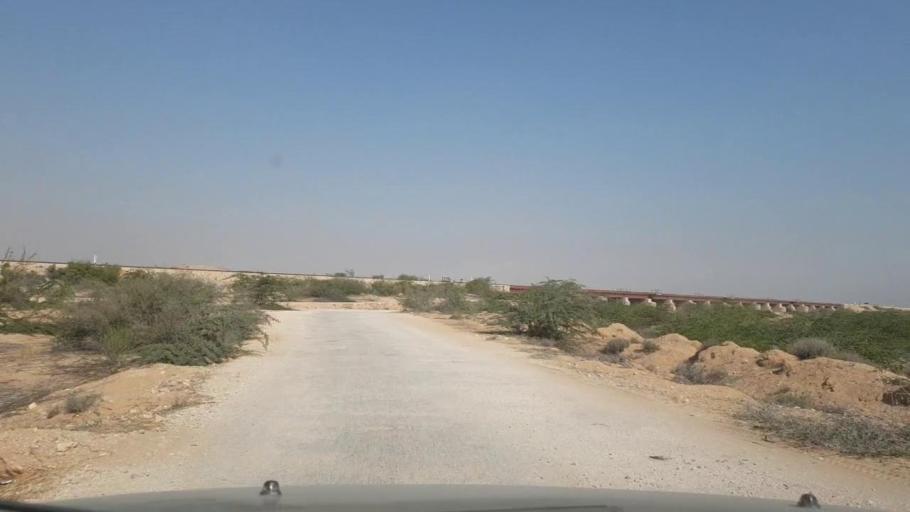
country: PK
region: Sindh
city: Thatta
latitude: 24.9811
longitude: 67.9872
